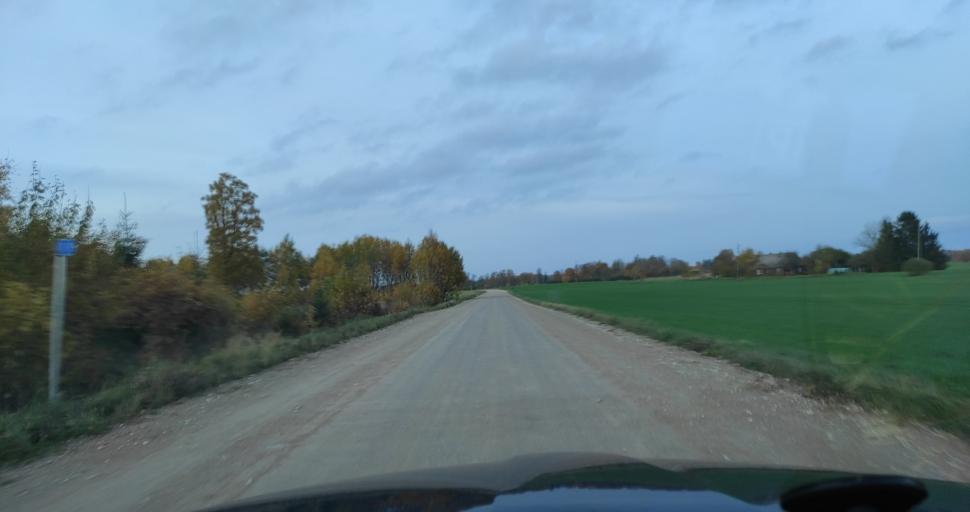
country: LV
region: Aizpute
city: Aizpute
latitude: 56.6769
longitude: 21.7922
